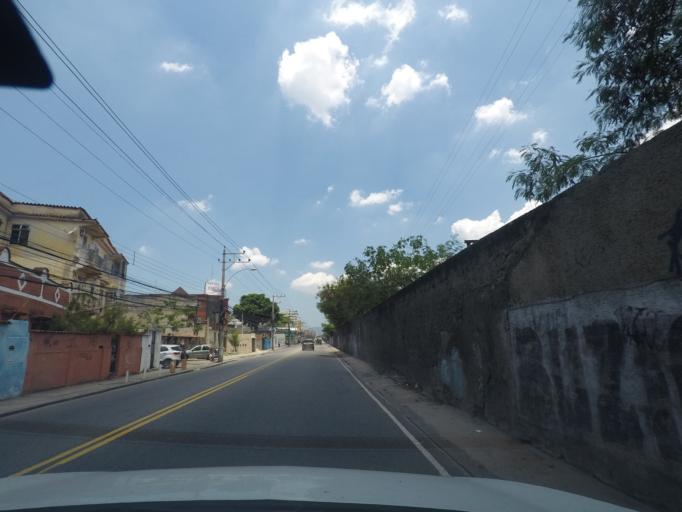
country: BR
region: Rio de Janeiro
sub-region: Sao Joao De Meriti
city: Sao Joao de Meriti
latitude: -22.8727
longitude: -43.3439
